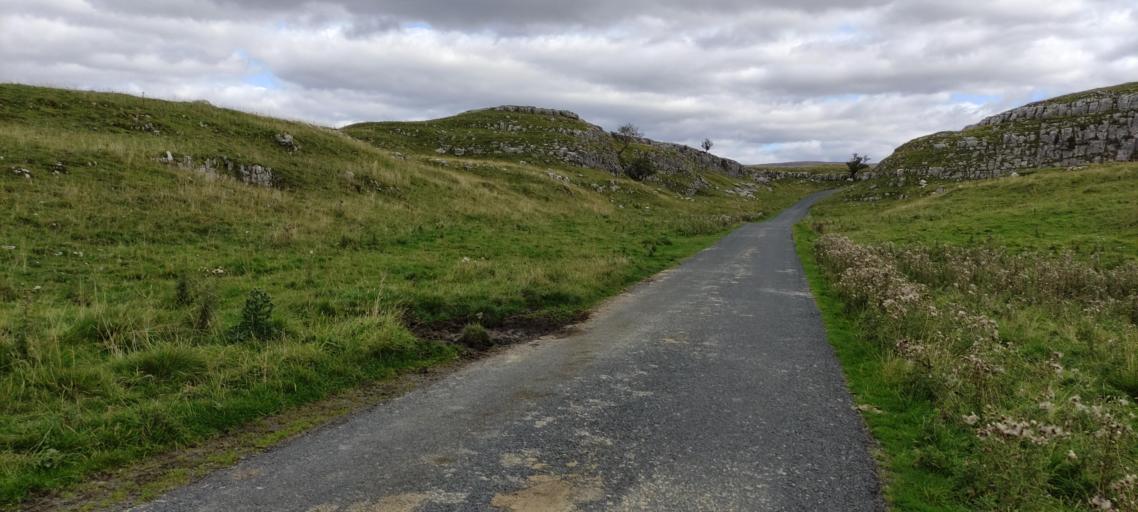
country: GB
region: England
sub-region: North Yorkshire
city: Settle
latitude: 54.0901
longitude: -2.2538
